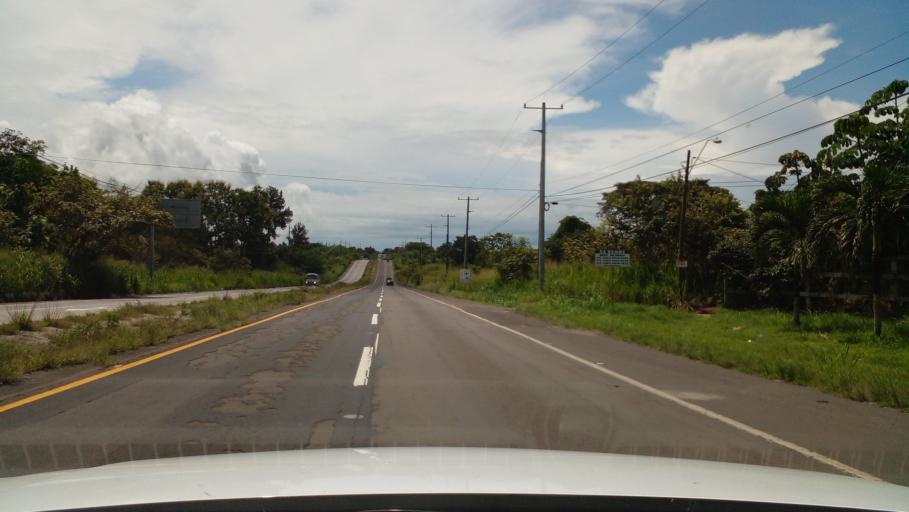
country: PA
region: Cocle
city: Rio Hato
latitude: 8.3877
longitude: -80.1096
